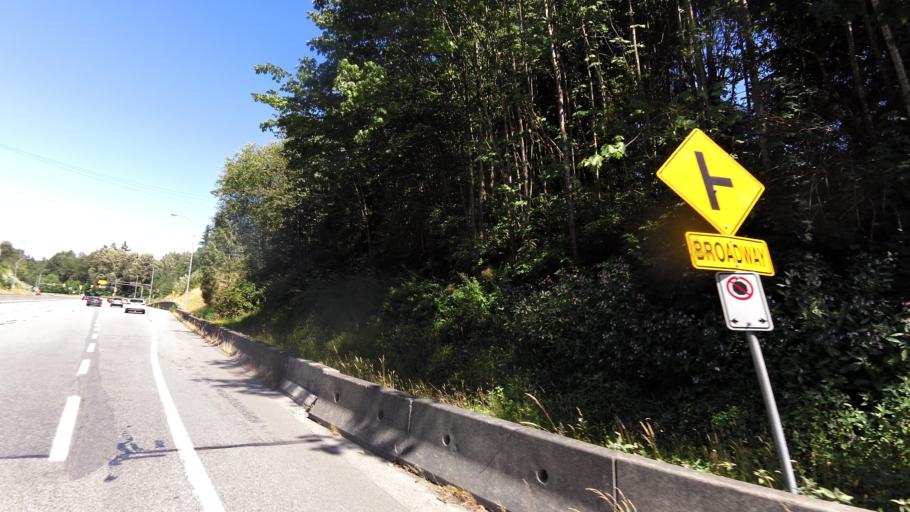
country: CA
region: British Columbia
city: Burnaby
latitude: 49.2624
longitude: -122.9037
